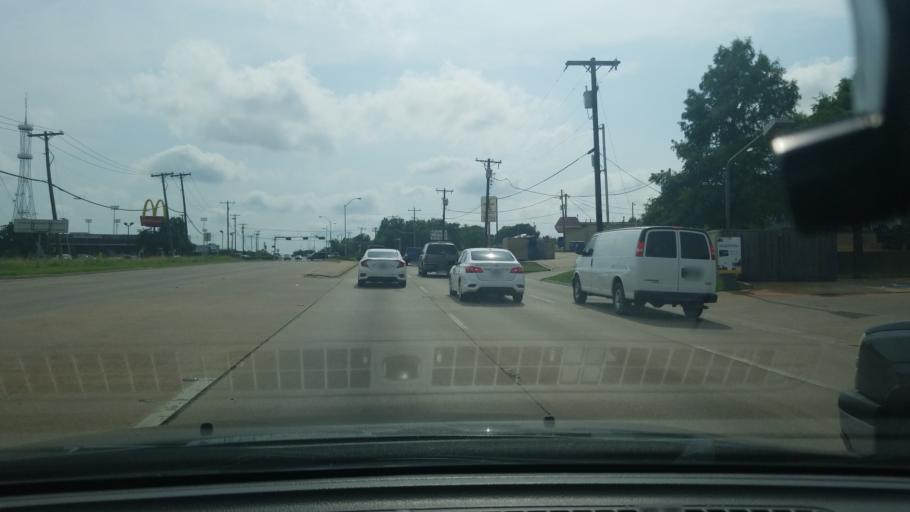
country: US
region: Texas
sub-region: Dallas County
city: Mesquite
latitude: 32.7673
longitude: -96.6278
